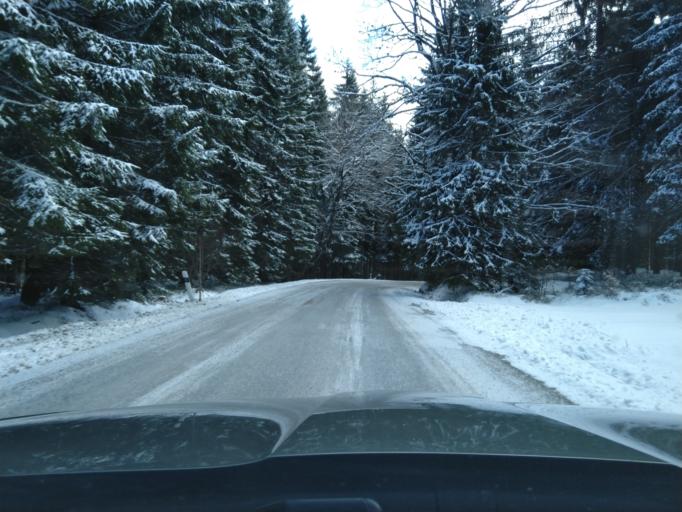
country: CZ
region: Jihocesky
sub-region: Okres Prachatice
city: Stachy
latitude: 49.0563
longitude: 13.6525
